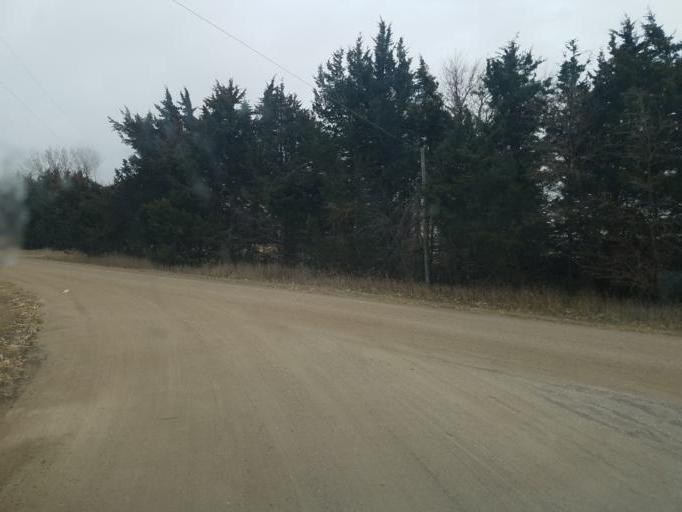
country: US
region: Nebraska
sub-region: Pierce County
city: Plainview
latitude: 42.4378
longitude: -97.7985
